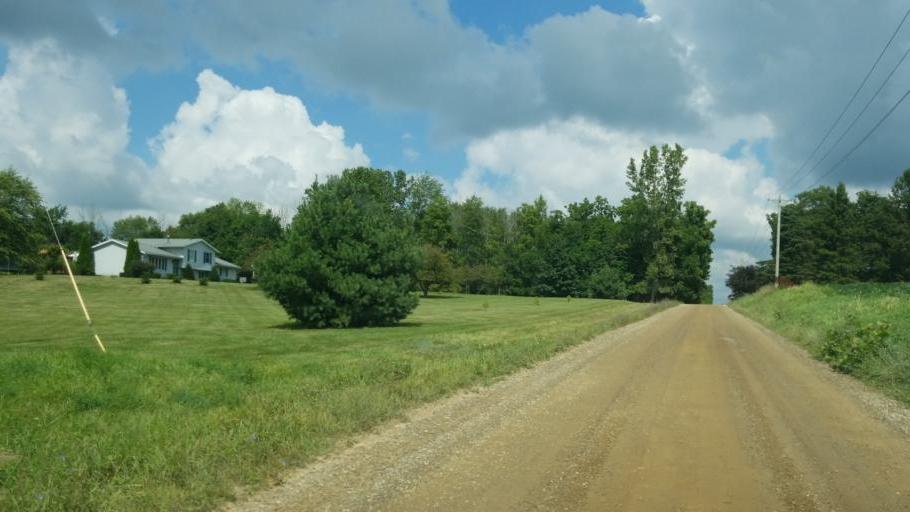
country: US
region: Ohio
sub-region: Knox County
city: Mount Vernon
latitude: 40.3166
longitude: -82.4926
